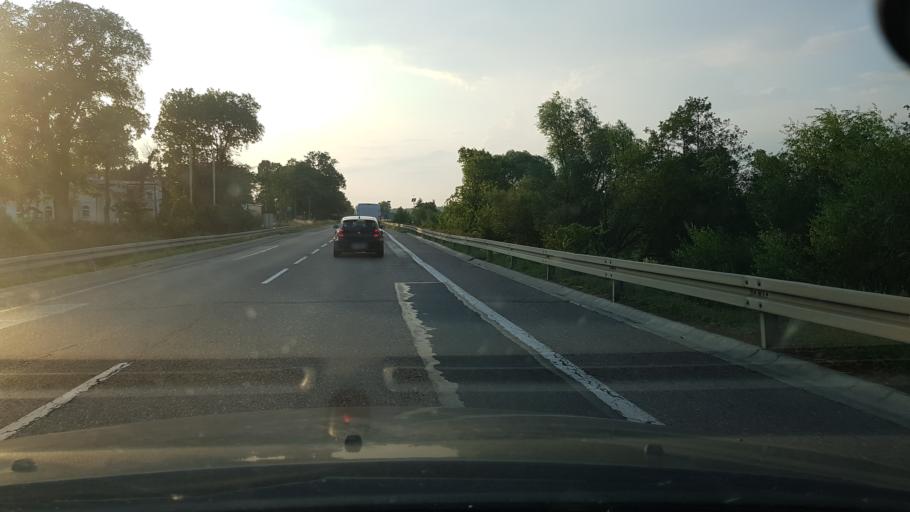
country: PL
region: Masovian Voivodeship
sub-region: Powiat plonski
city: Baboszewo
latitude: 52.7025
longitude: 20.3375
